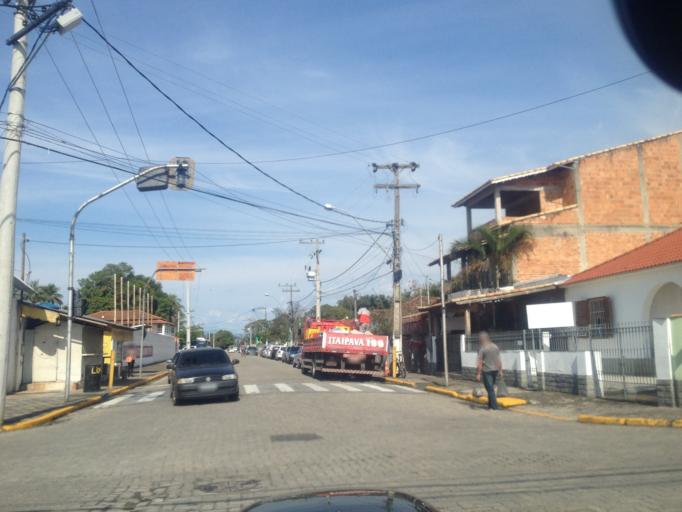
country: BR
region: Rio de Janeiro
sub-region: Porto Real
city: Porto Real
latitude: -22.4203
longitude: -44.2891
